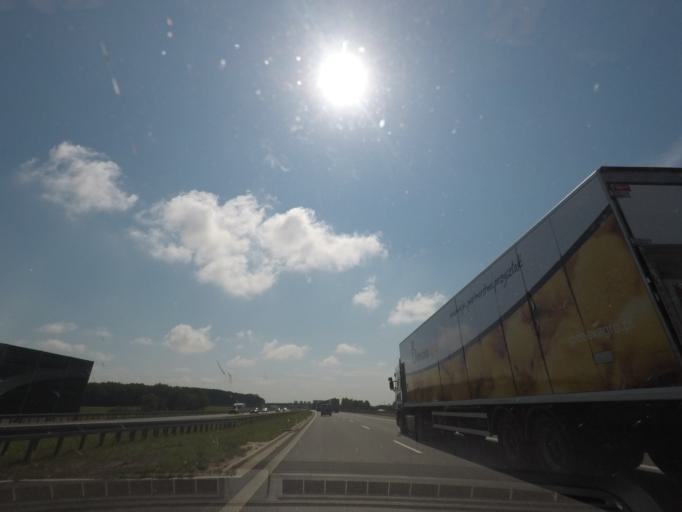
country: PL
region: Kujawsko-Pomorskie
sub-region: Powiat wloclawski
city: Baruchowo
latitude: 52.4445
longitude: 19.2300
